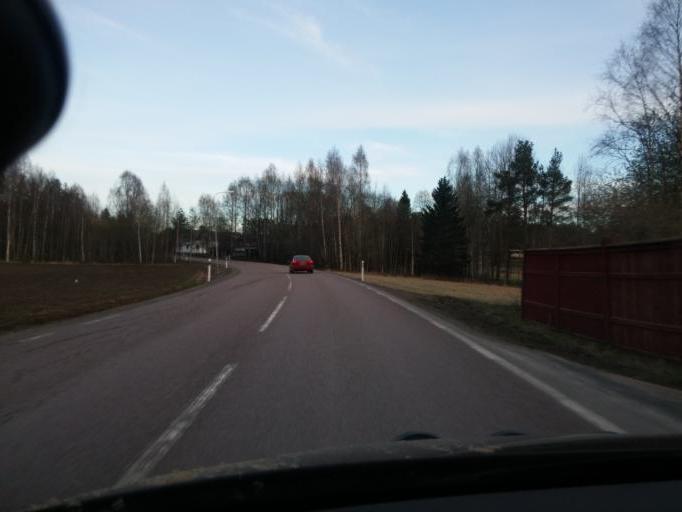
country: SE
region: Gaevleborg
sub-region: Ljusdals Kommun
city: Ljusdal
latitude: 61.8387
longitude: 16.0024
